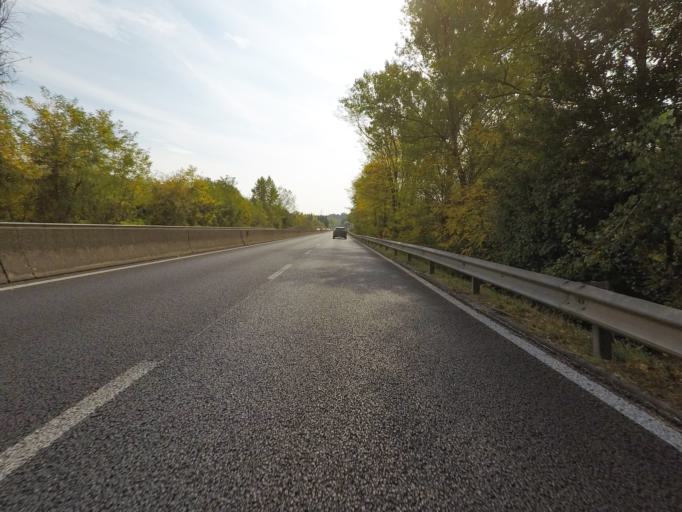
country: IT
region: Tuscany
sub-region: Provincia di Siena
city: Belverde
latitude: 43.3252
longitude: 11.2968
